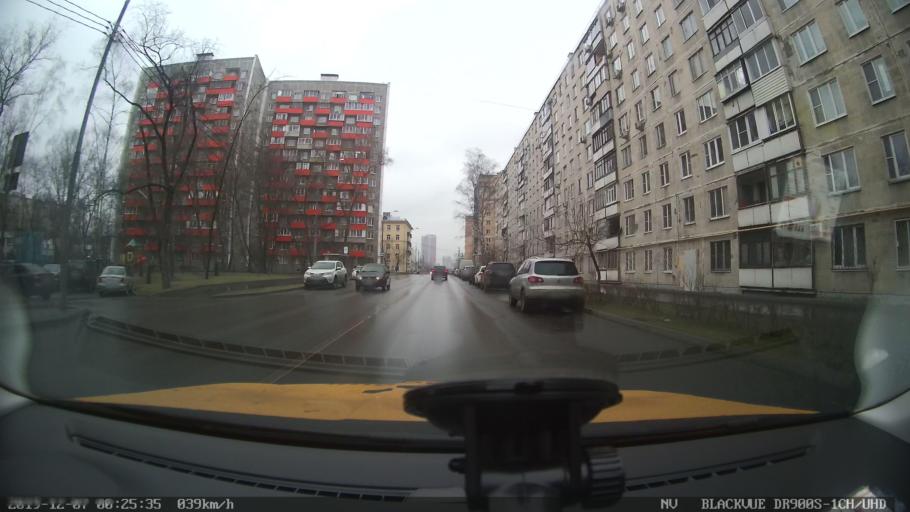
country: RU
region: Moscow
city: Rostokino
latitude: 55.8309
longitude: 37.6629
